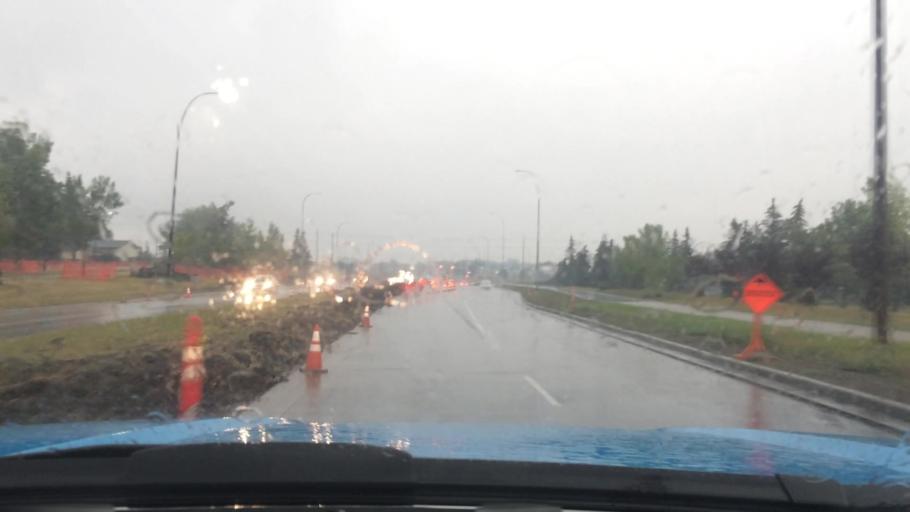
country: CA
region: Alberta
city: Calgary
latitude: 51.0930
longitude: -113.9584
